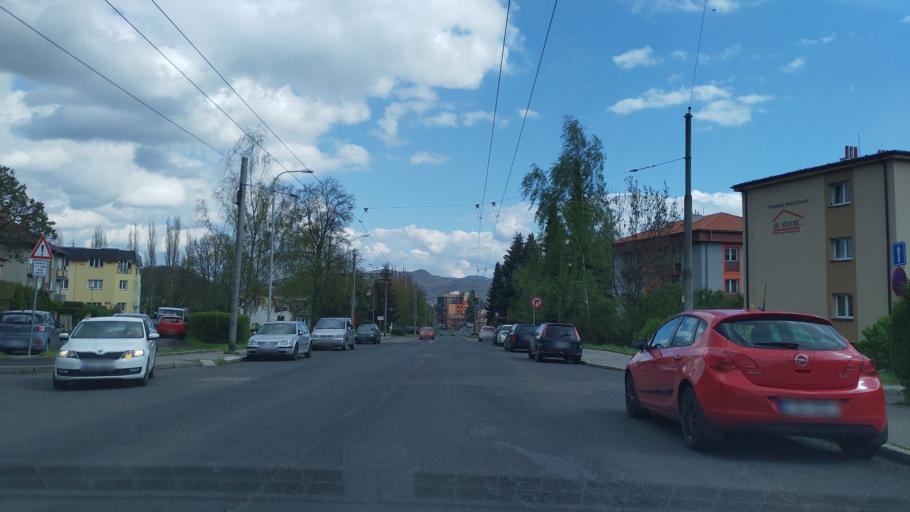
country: CZ
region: Ustecky
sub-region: Okres Usti nad Labem
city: Usti nad Labem
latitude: 50.6827
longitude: 14.0025
